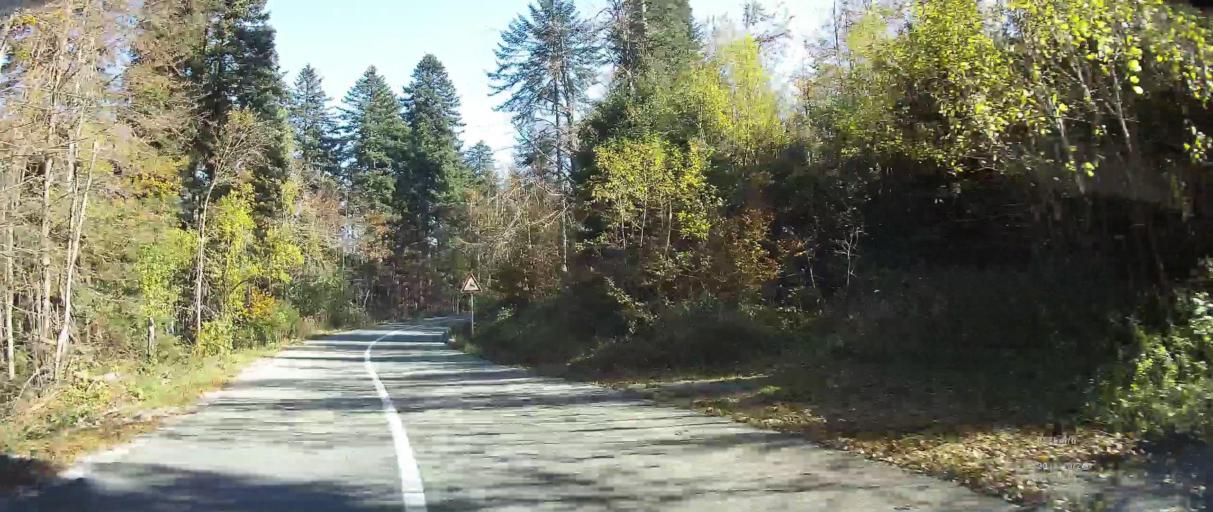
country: HR
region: Primorsko-Goranska
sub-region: Grad Delnice
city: Delnice
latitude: 45.3969
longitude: 14.6931
